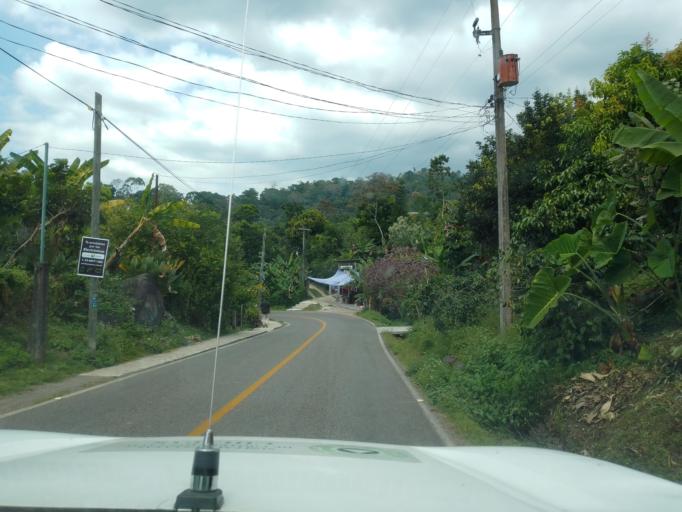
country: MX
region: Chiapas
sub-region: Union Juarez
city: Santo Domingo
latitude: 15.0375
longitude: -92.1154
